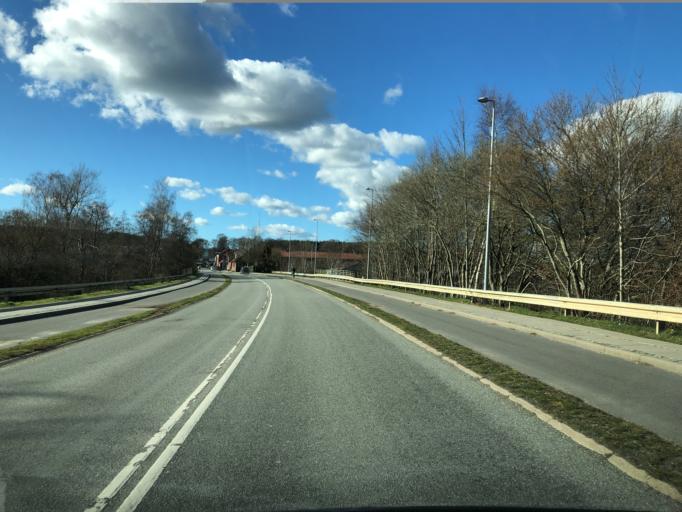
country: DK
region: Central Jutland
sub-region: Favrskov Kommune
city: Hinnerup
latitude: 56.2624
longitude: 10.0668
